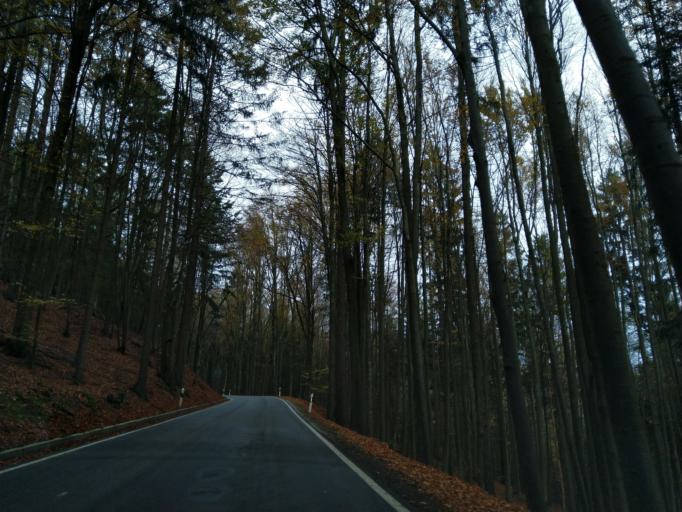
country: DE
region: Bavaria
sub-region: Lower Bavaria
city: Zenting
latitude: 48.7995
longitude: 13.2361
